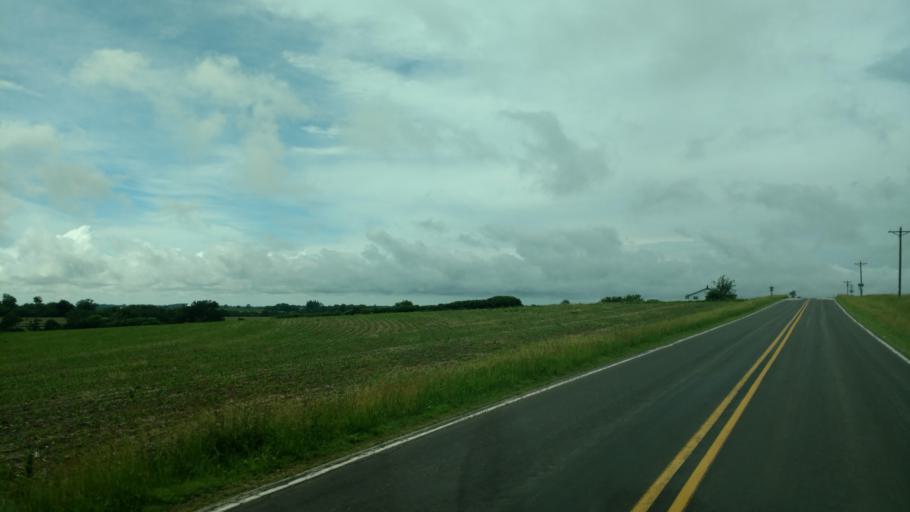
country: US
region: Wisconsin
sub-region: Vernon County
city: Hillsboro
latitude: 43.7245
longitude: -90.4479
